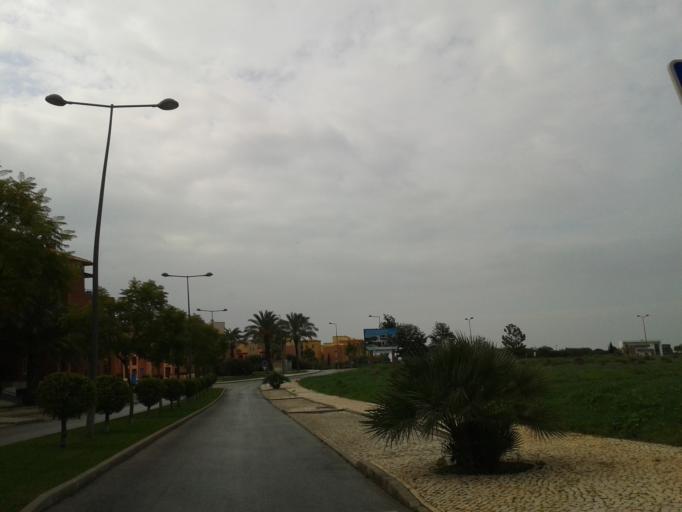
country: PT
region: Faro
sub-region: Loule
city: Boliqueime
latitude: 37.1073
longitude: -8.1402
